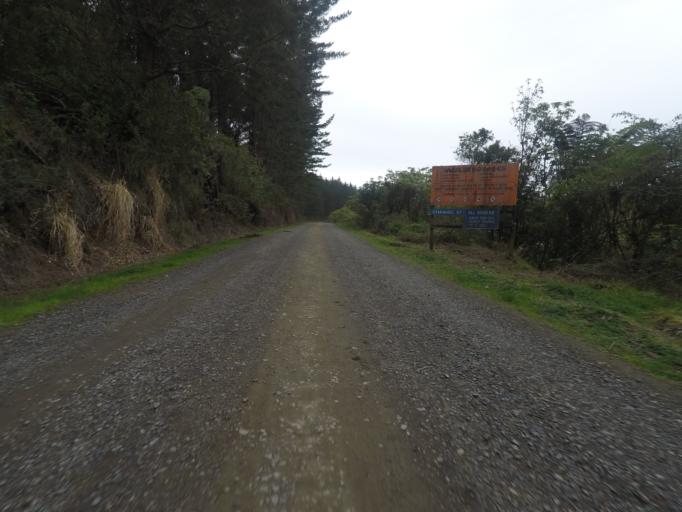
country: NZ
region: Auckland
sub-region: Auckland
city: Muriwai Beach
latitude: -36.7514
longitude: 174.5752
